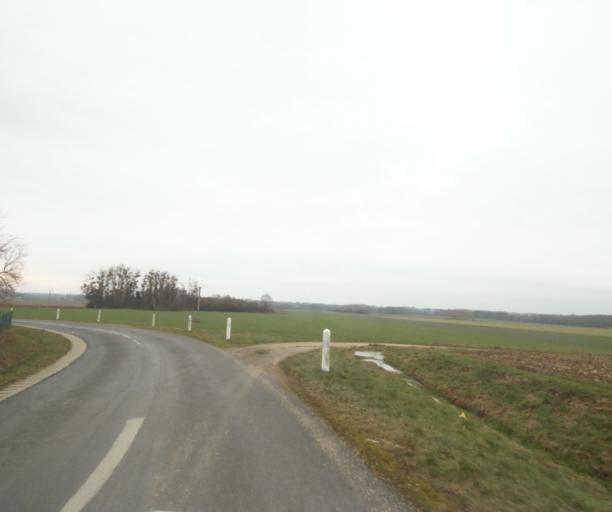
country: FR
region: Champagne-Ardenne
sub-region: Departement de la Haute-Marne
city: Villiers-en-Lieu
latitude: 48.6341
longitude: 4.7689
